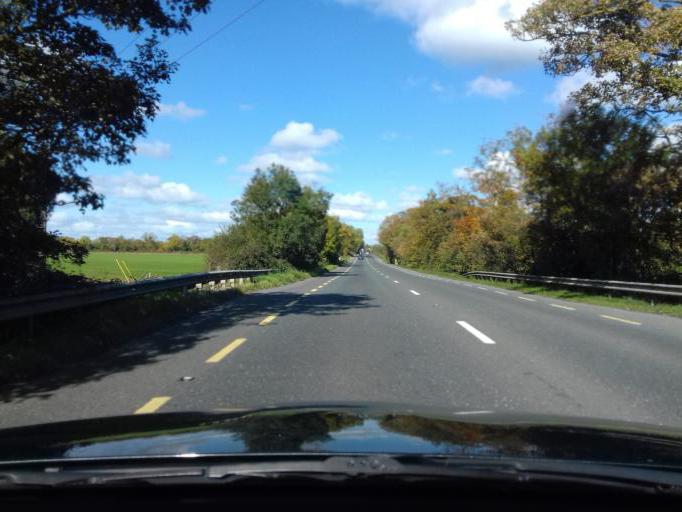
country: IE
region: Leinster
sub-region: An Mhi
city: Ashbourne
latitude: 53.5405
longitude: -6.4271
